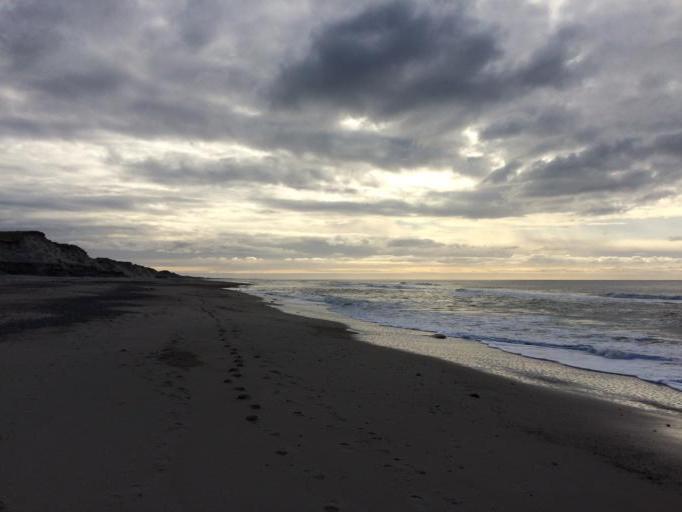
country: DK
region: Central Jutland
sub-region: Holstebro Kommune
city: Ulfborg
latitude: 56.2944
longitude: 8.1246
